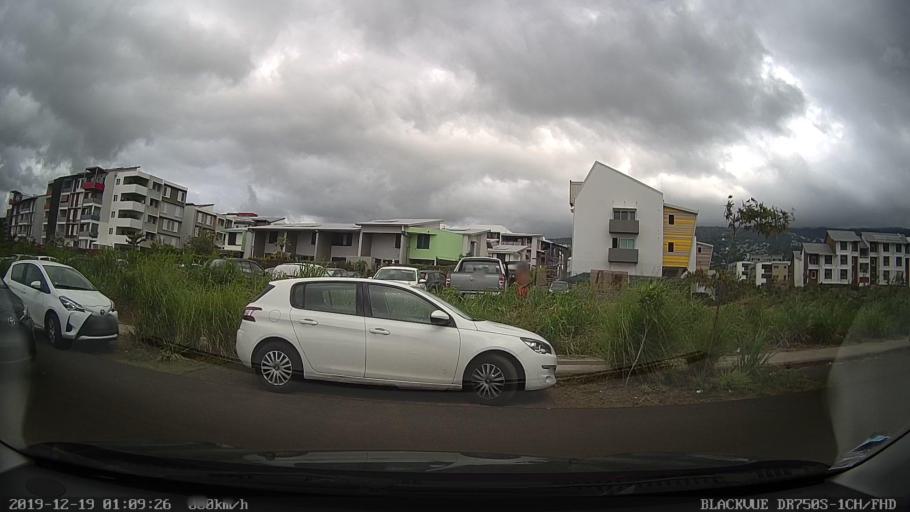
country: RE
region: Reunion
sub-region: Reunion
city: Sainte-Marie
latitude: -20.9208
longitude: 55.5273
